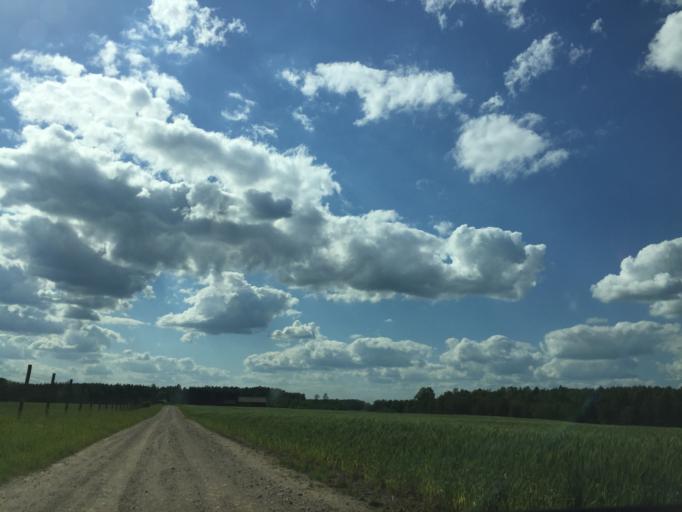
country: LV
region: Jaunpils
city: Jaunpils
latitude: 56.8080
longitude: 23.0882
